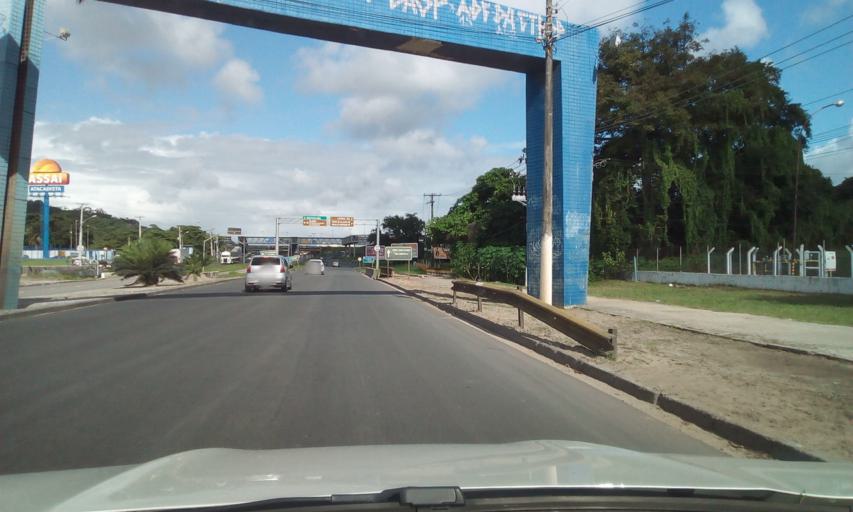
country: BR
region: Pernambuco
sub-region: Abreu E Lima
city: Abreu e Lima
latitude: -7.9179
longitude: -34.8967
